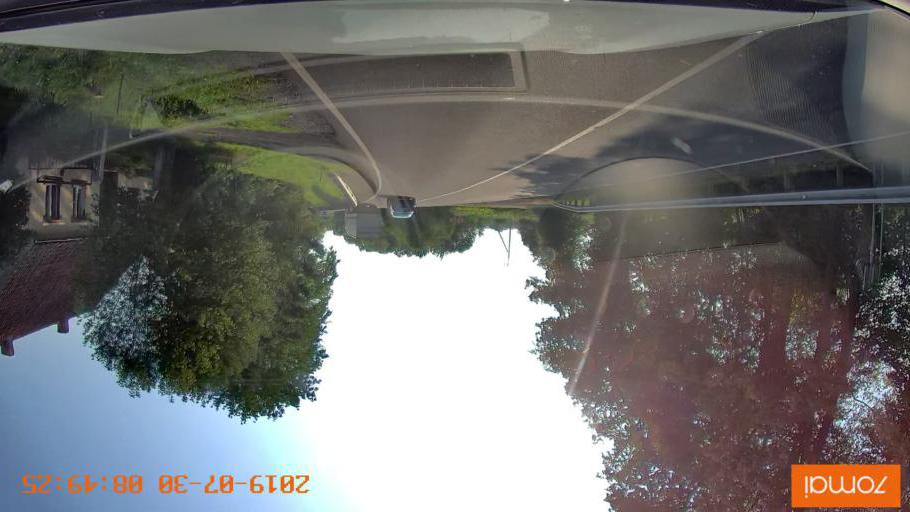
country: RU
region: Kaliningrad
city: Chernyakhovsk
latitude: 54.6136
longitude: 21.9216
